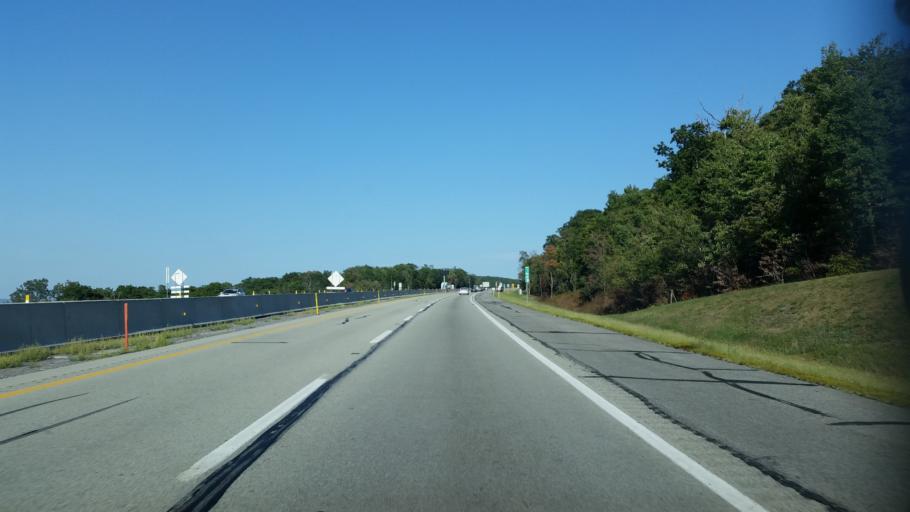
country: US
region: Pennsylvania
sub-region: Bedford County
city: Earlston
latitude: 40.0282
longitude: -78.1730
